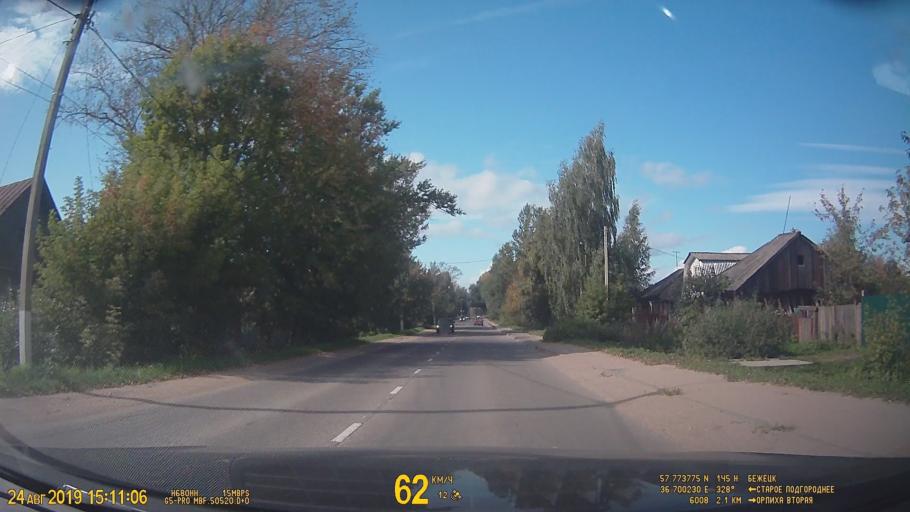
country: RU
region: Tverskaya
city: Bezhetsk
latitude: 57.7739
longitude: 36.7001
